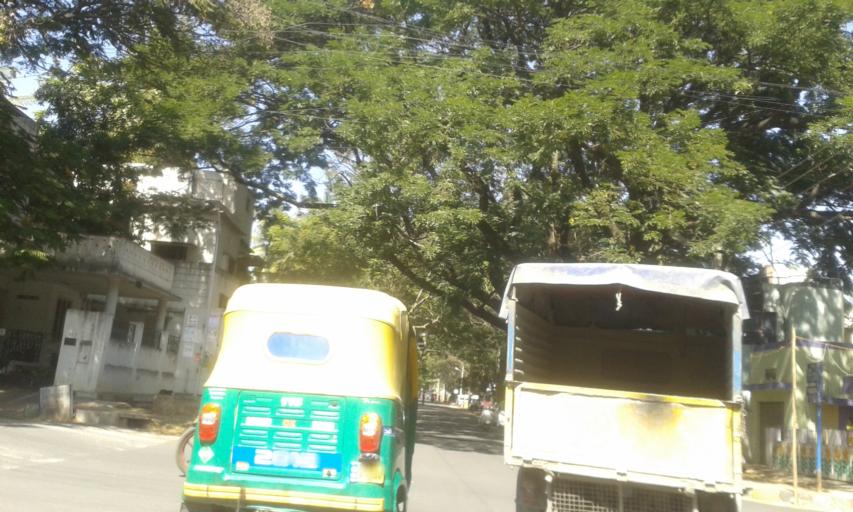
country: IN
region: Karnataka
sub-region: Bangalore Urban
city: Bangalore
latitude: 12.9205
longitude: 77.5915
